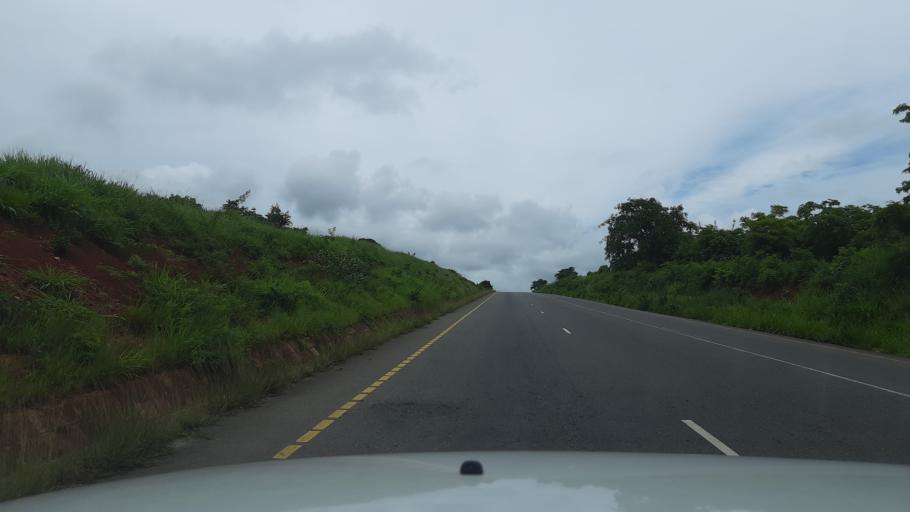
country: TZ
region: Pwani
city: Lugoba
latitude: -6.0380
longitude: 38.2398
